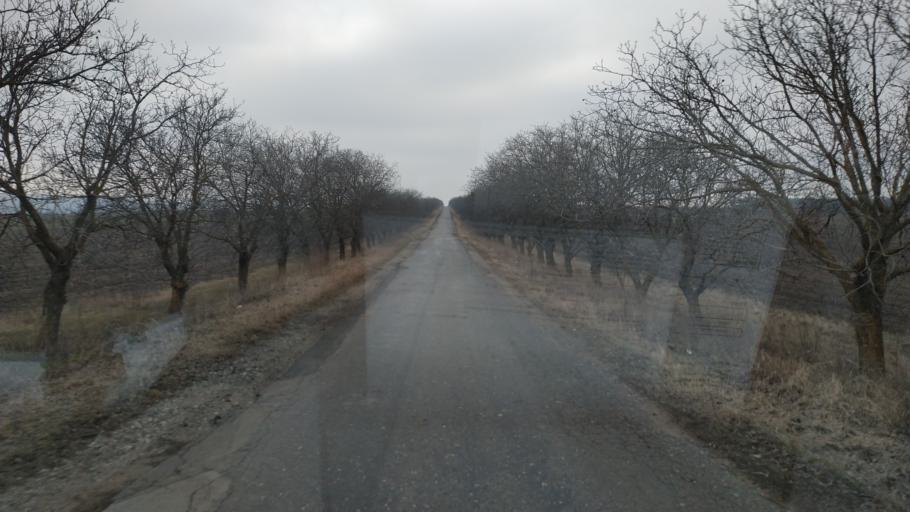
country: MD
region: Hincesti
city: Dancu
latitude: 46.9001
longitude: 28.3049
